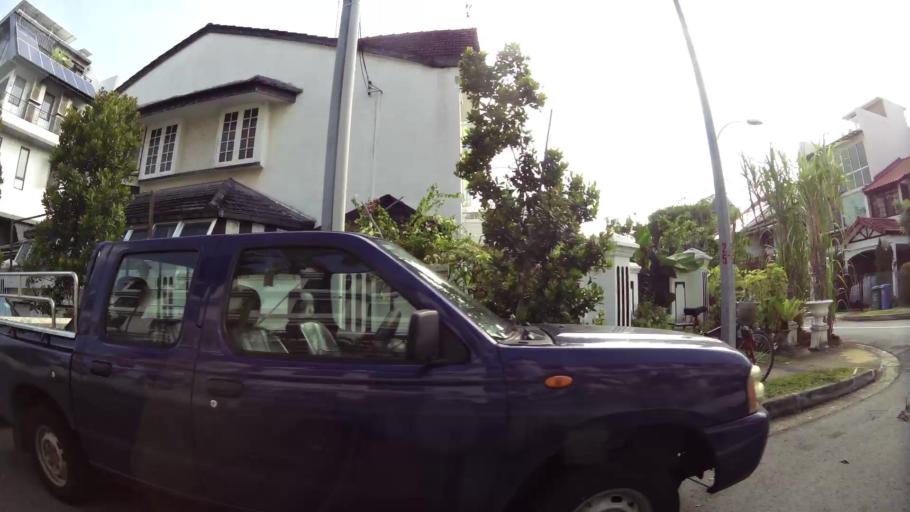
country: SG
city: Singapore
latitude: 1.3207
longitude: 103.9076
